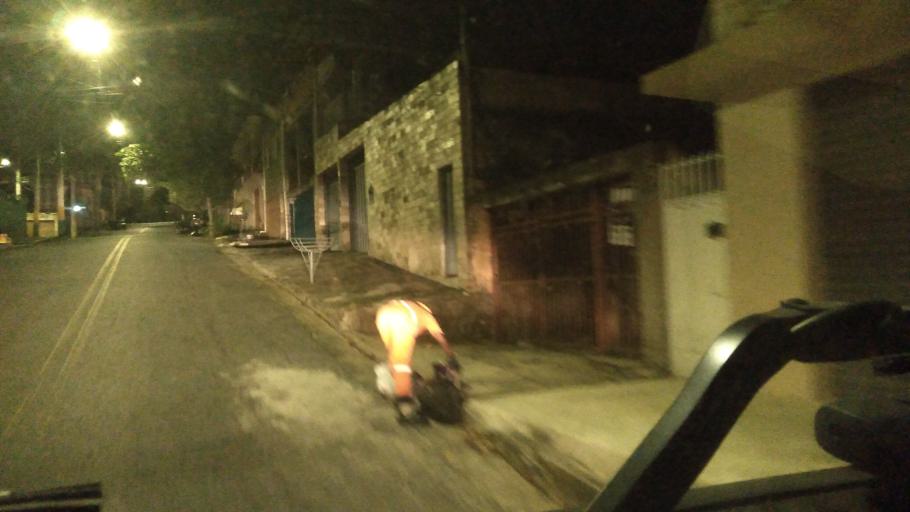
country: BR
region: Minas Gerais
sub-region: Belo Horizonte
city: Belo Horizonte
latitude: -19.8747
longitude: -43.9394
